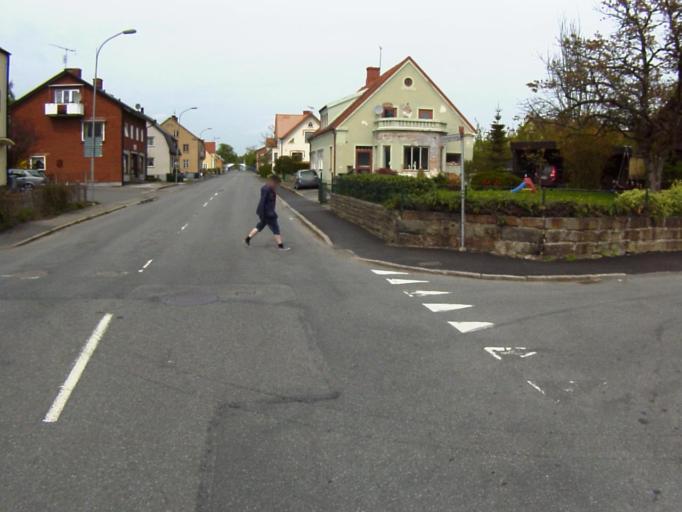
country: SE
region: Skane
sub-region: Kristianstads Kommun
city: Onnestad
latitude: 55.9313
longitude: 13.9724
